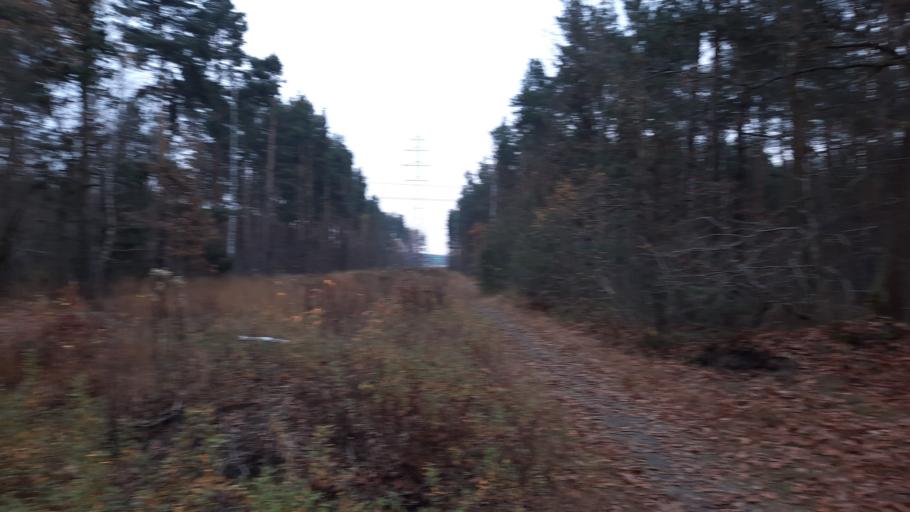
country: PL
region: Masovian Voivodeship
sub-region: Powiat wolominski
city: Zabki
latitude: 52.2916
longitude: 21.1324
